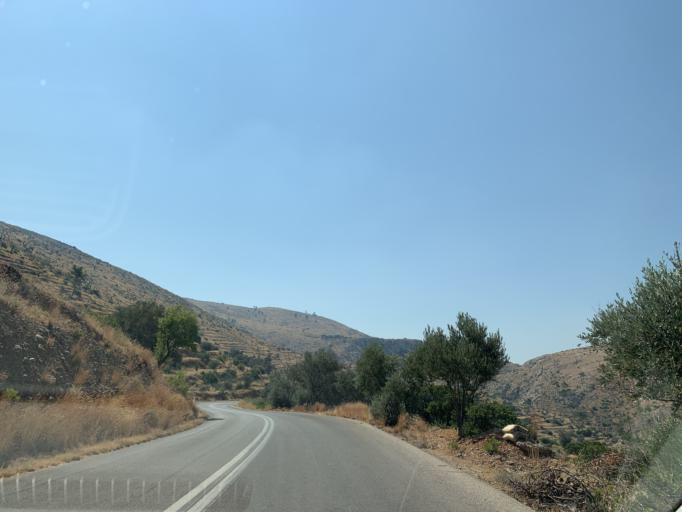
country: GR
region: North Aegean
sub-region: Chios
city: Thymiana
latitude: 38.3250
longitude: 26.0031
